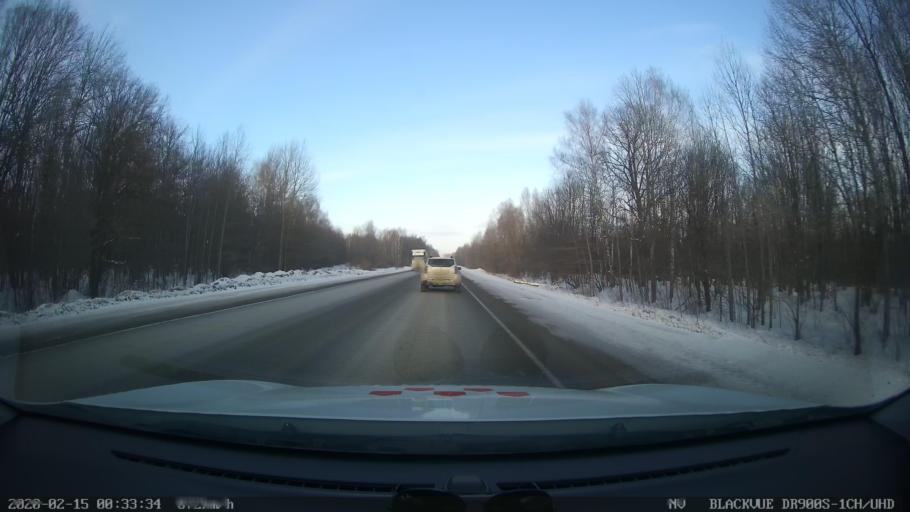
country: RU
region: Tatarstan
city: Verkhniy Uslon
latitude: 55.6902
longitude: 48.8751
